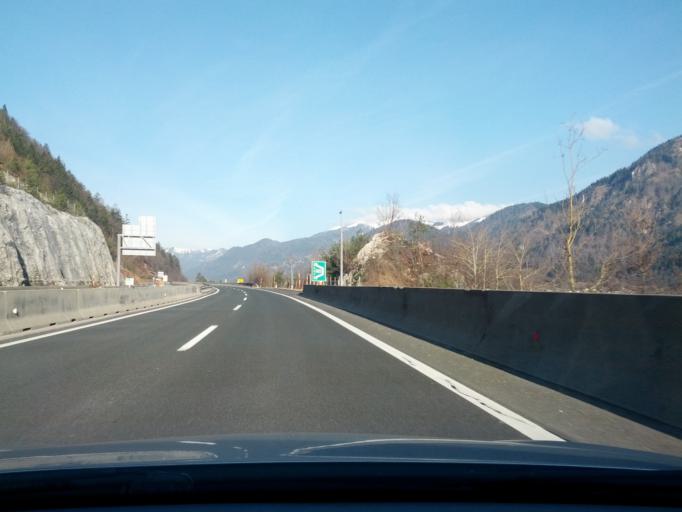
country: SI
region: Jesenice
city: Slovenski Javornik
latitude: 46.4197
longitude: 14.0866
